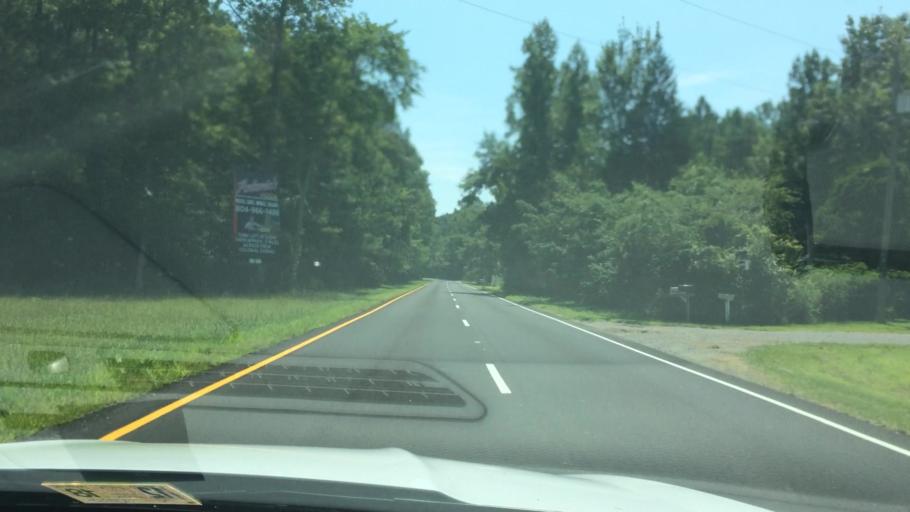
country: US
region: Virginia
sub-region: Charles City County
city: Charles City
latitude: 37.4526
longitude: -77.0790
